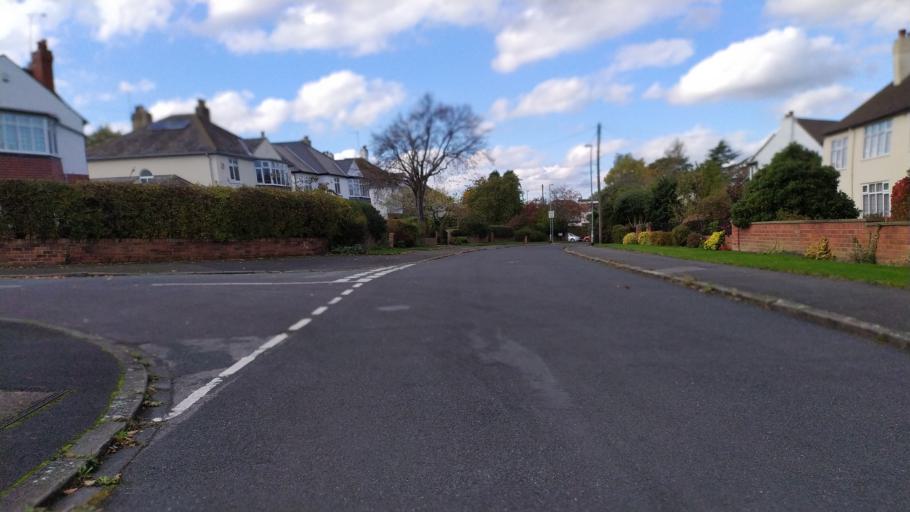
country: GB
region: England
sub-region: City and Borough of Leeds
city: Horsforth
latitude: 53.8299
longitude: -1.5955
